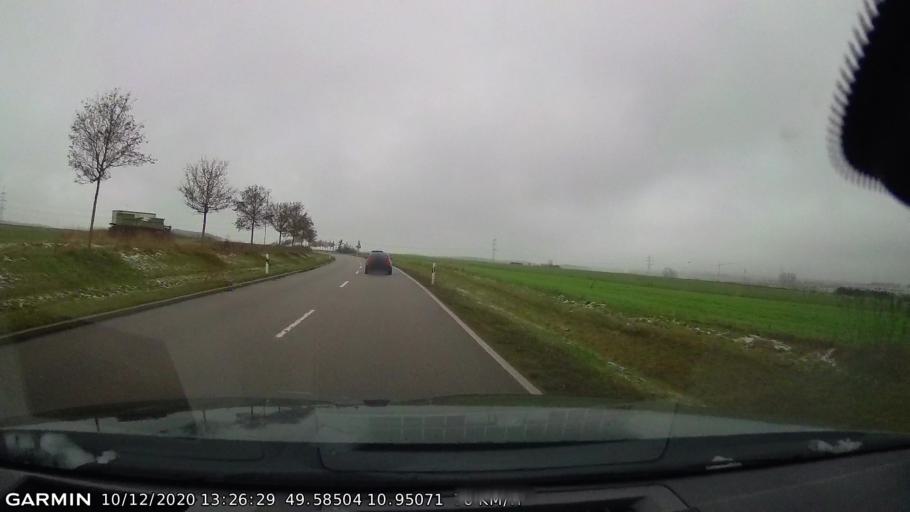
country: DE
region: Bavaria
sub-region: Regierungsbezirk Mittelfranken
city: Erlangen
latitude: 49.5851
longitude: 10.9504
